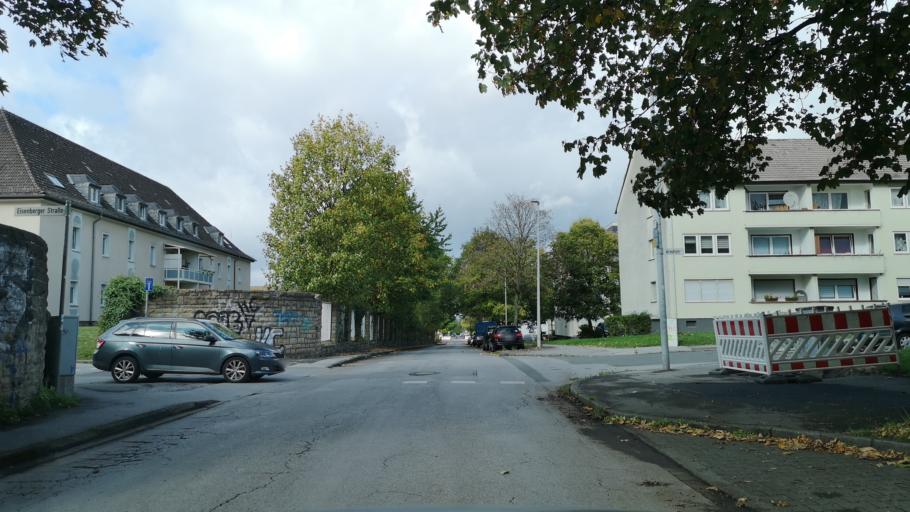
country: DE
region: North Rhine-Westphalia
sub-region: Regierungsbezirk Arnsberg
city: Menden
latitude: 51.4424
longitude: 7.7745
